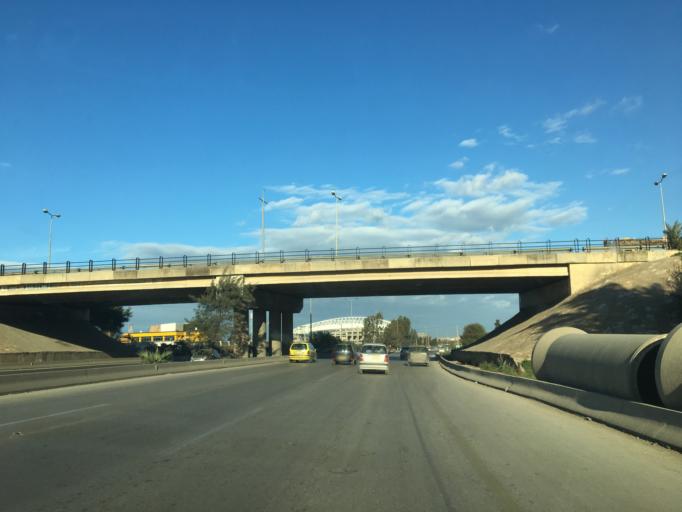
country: DZ
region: Tipaza
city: Baraki
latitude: 36.6864
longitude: 3.1137
